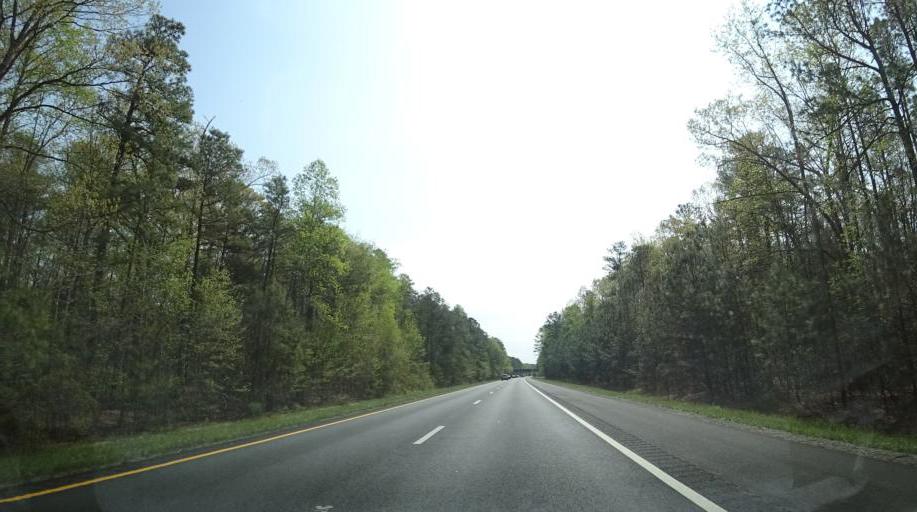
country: US
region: Virginia
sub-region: New Kent County
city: New Kent
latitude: 37.4797
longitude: -76.9246
